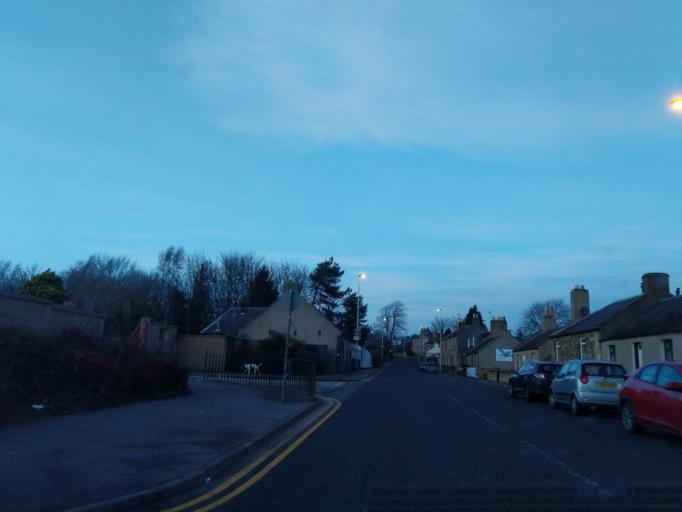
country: GB
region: Scotland
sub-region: Midlothian
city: Bonnyrigg
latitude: 55.8776
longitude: -3.1076
